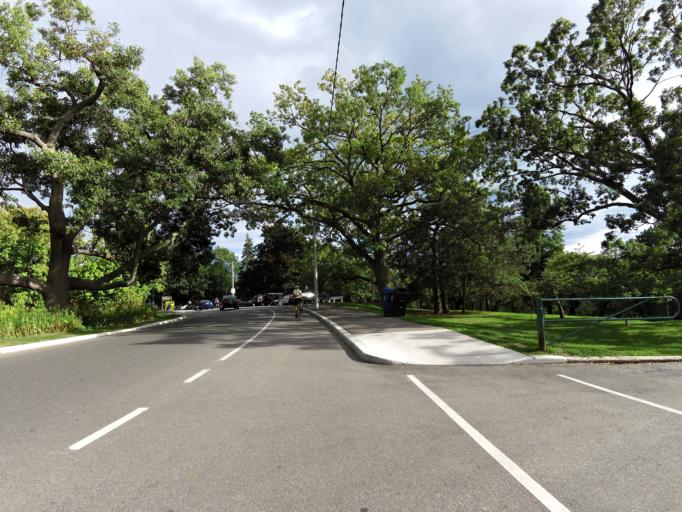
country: CA
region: Ontario
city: Toronto
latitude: 43.6458
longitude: -79.4672
